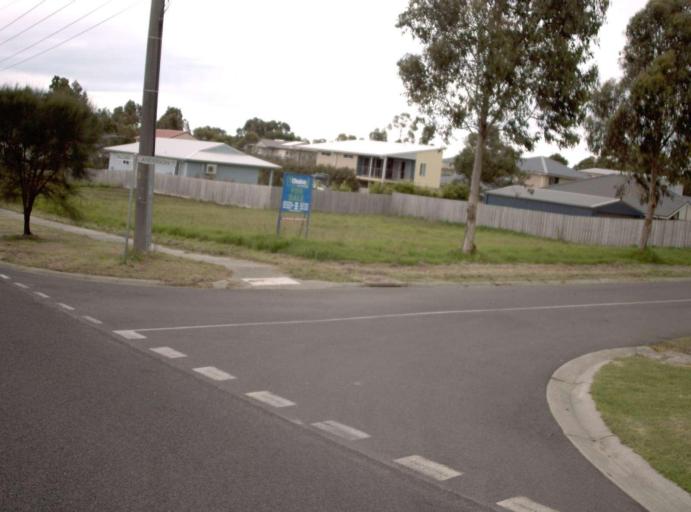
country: AU
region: Victoria
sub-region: Bass Coast
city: Cowes
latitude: -38.4126
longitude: 145.4326
